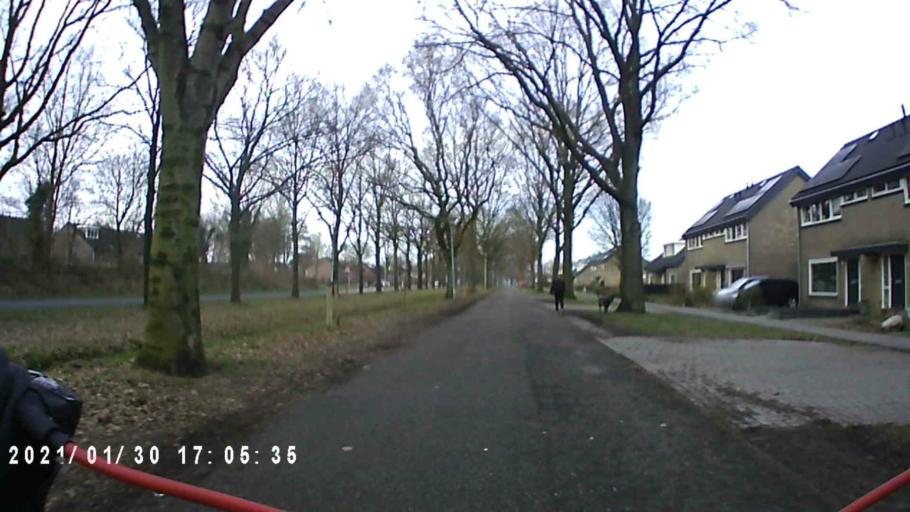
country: NL
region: Groningen
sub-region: Gemeente Leek
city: Leek
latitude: 53.1587
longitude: 6.3688
